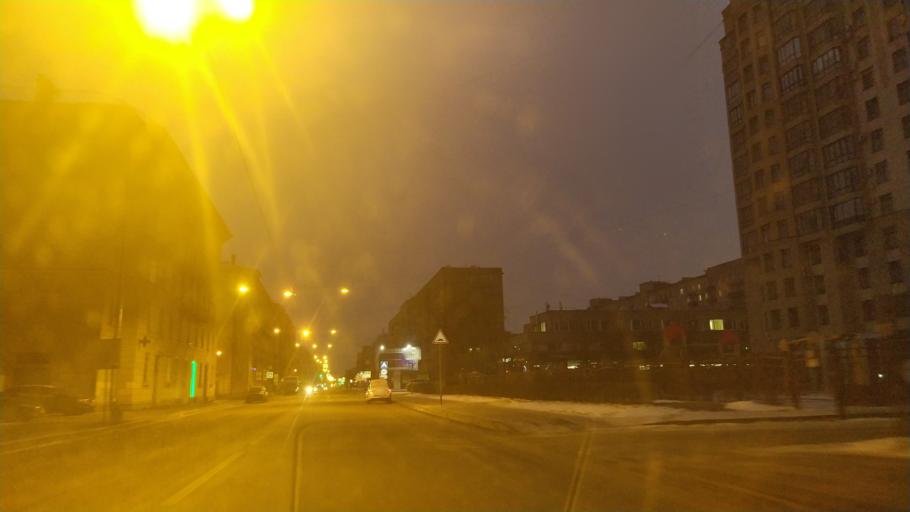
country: RU
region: Leningrad
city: Kalininskiy
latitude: 59.9565
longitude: 30.4107
